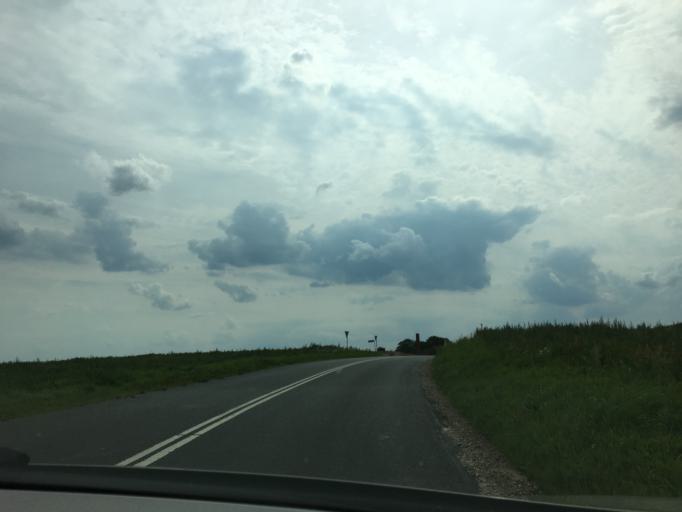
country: DK
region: Central Jutland
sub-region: Viborg Kommune
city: Stoholm
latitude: 56.4660
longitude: 9.1448
